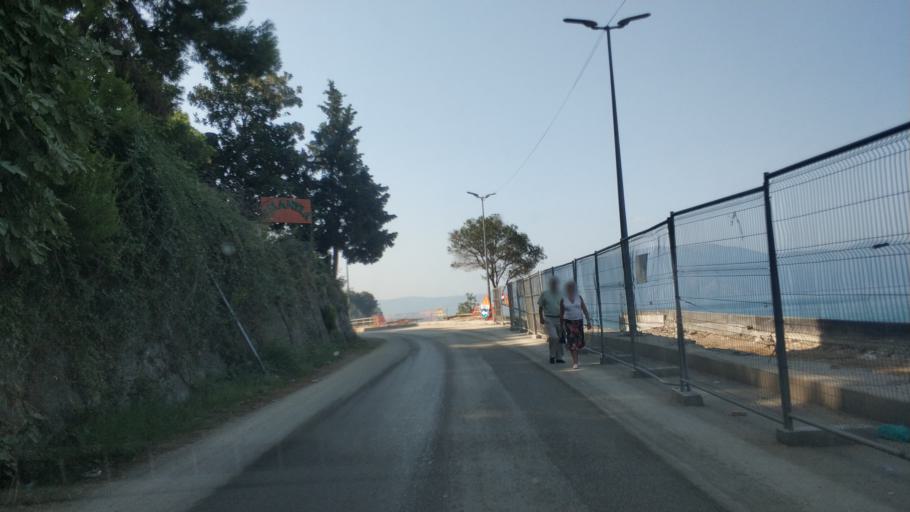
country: AL
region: Vlore
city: Vlore
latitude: 40.4239
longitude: 19.4900
